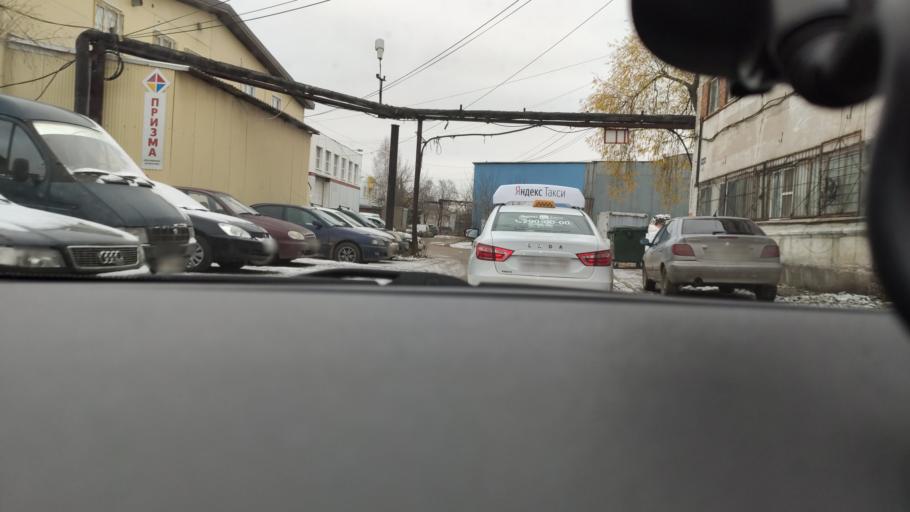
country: RU
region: Perm
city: Perm
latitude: 57.9851
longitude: 56.2751
